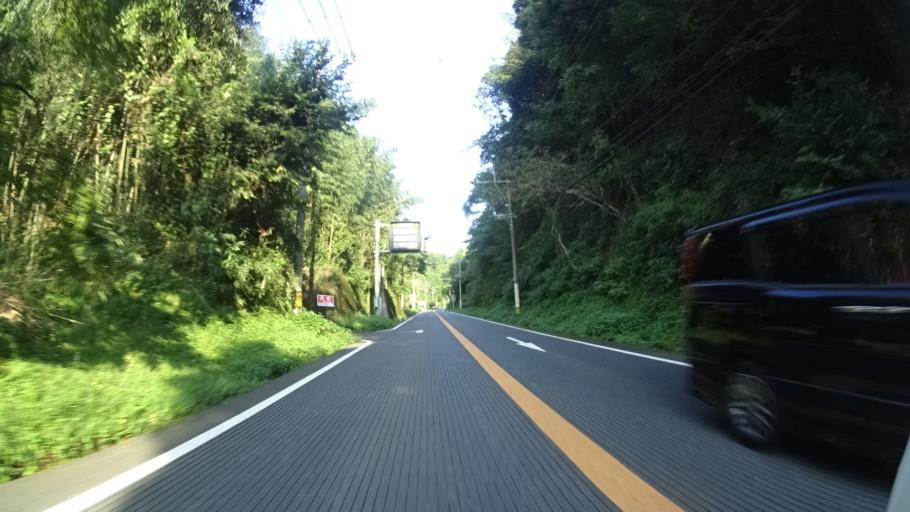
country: JP
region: Oita
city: Bungo-Takada-shi
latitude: 33.4459
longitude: 131.3360
